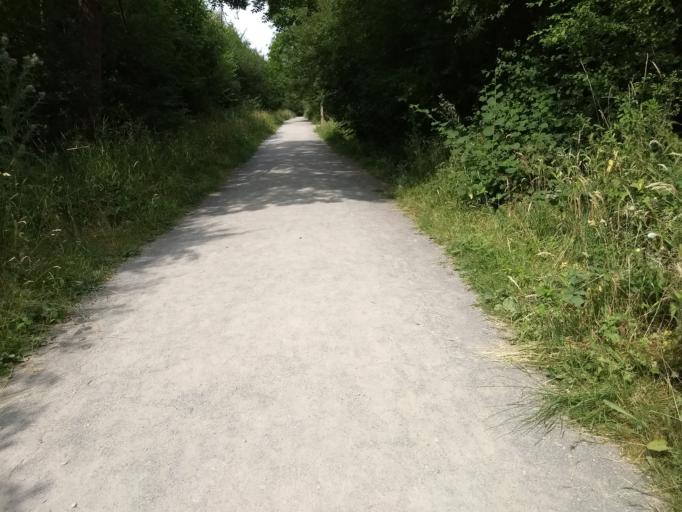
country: GB
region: England
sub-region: Northamptonshire
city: Hartwell
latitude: 52.1593
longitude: -0.8384
